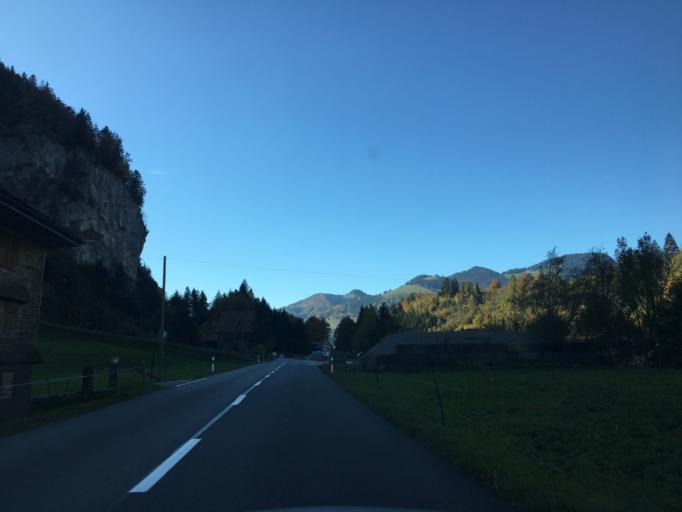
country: CH
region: Fribourg
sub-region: Gruyere District
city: Charmey
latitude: 46.6101
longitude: 7.1829
